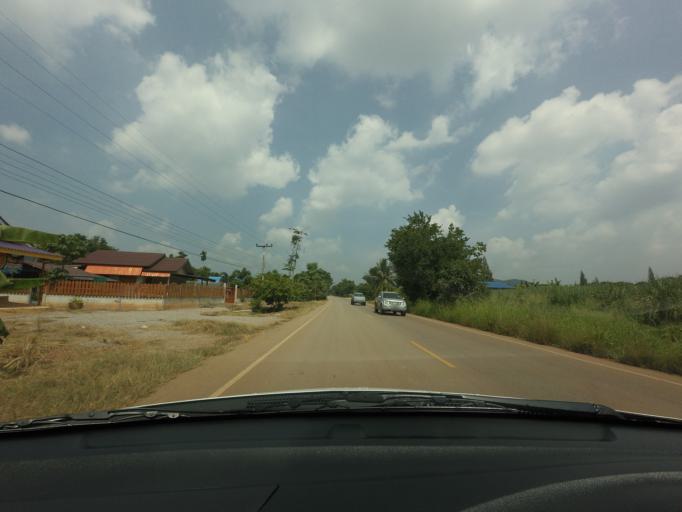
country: TH
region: Nakhon Ratchasima
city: Pak Chong
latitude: 14.5630
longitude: 101.5716
